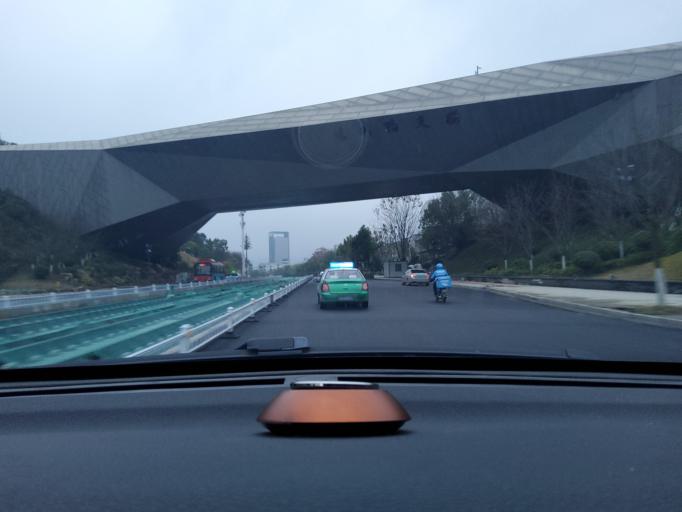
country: CN
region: Hubei
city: Tuanchengshan
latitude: 30.1941
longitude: 115.0226
